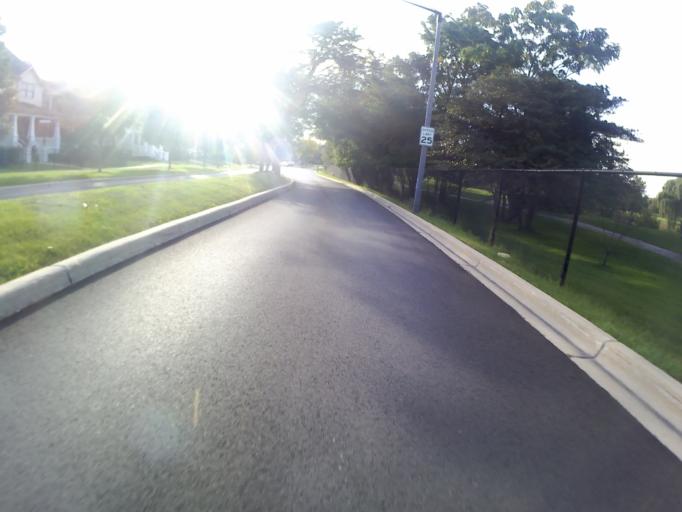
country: US
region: Illinois
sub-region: DuPage County
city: Lisle
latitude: 41.7770
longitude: -88.0728
